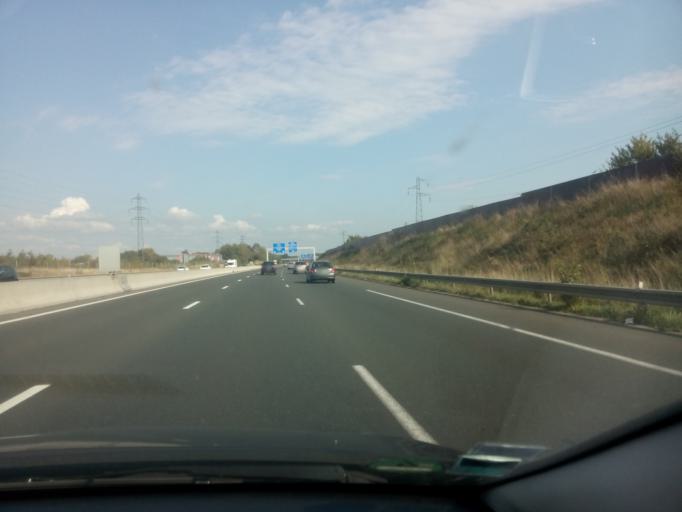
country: FR
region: Pays de la Loire
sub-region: Departement de Maine-et-Loire
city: Ecouflant
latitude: 47.4997
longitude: -0.5145
